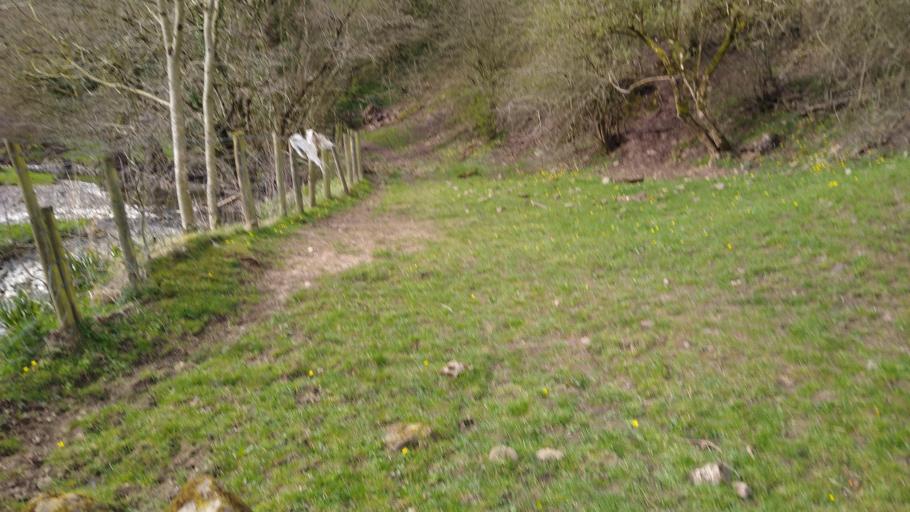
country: GB
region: England
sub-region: Cumbria
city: Dearham
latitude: 54.6753
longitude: -3.4093
